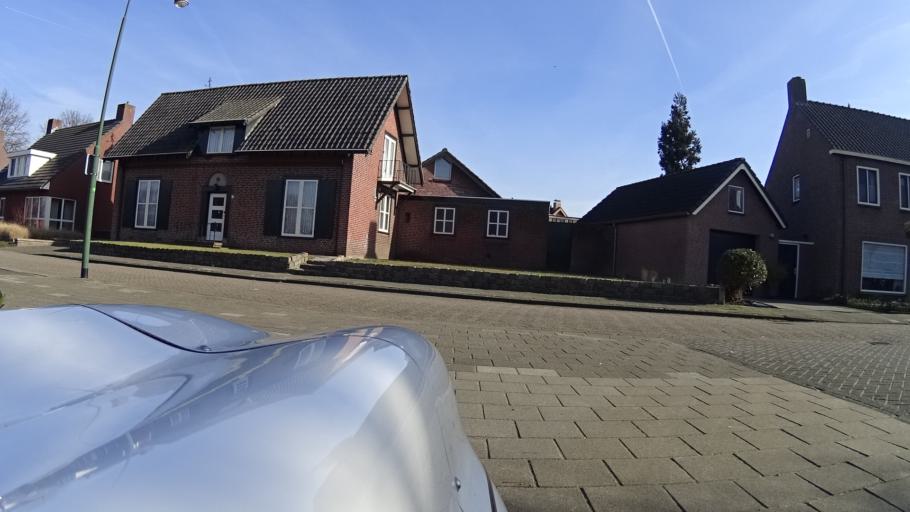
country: NL
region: North Brabant
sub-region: Gemeente Veghel
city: Erp
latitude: 51.5971
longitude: 5.6140
